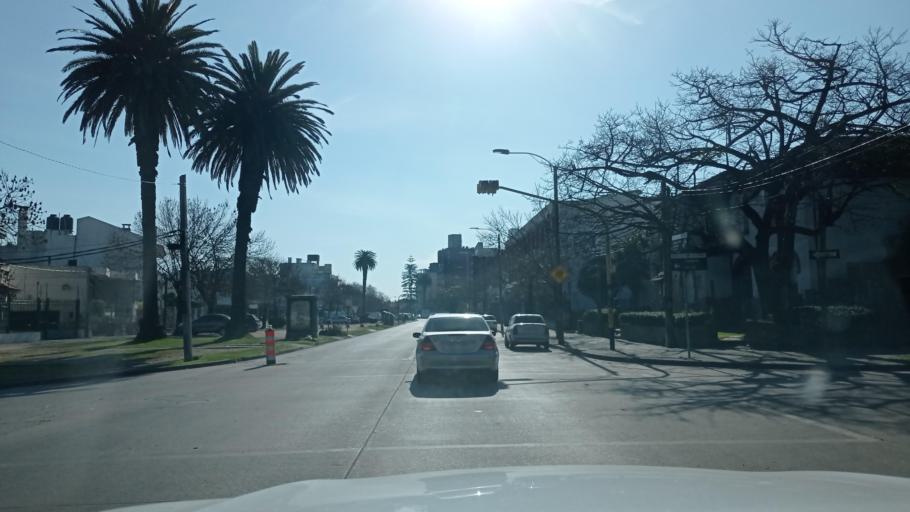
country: UY
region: Montevideo
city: Montevideo
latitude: -34.8760
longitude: -56.1577
